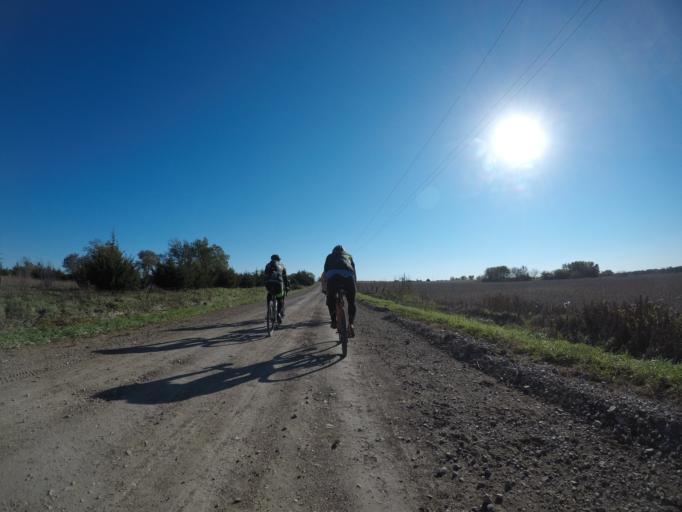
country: US
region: Kansas
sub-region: Morris County
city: Council Grove
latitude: 38.8260
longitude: -96.4745
